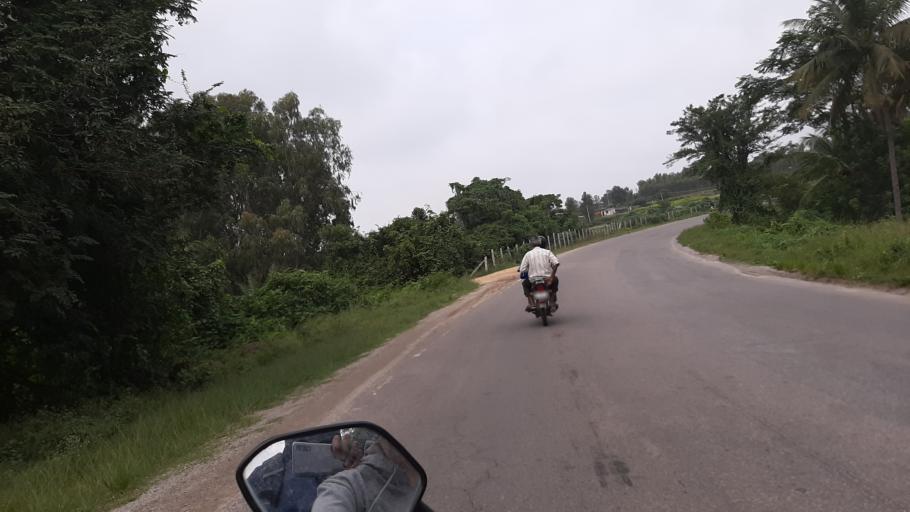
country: IN
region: Karnataka
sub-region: Bangalore Rural
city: Nelamangala
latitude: 12.9648
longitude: 77.3861
